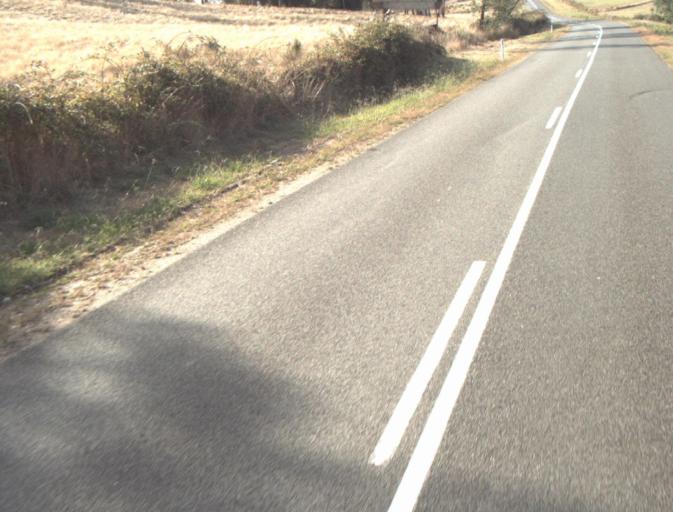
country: AU
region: Tasmania
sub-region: Launceston
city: Mayfield
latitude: -41.2193
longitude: 147.1215
